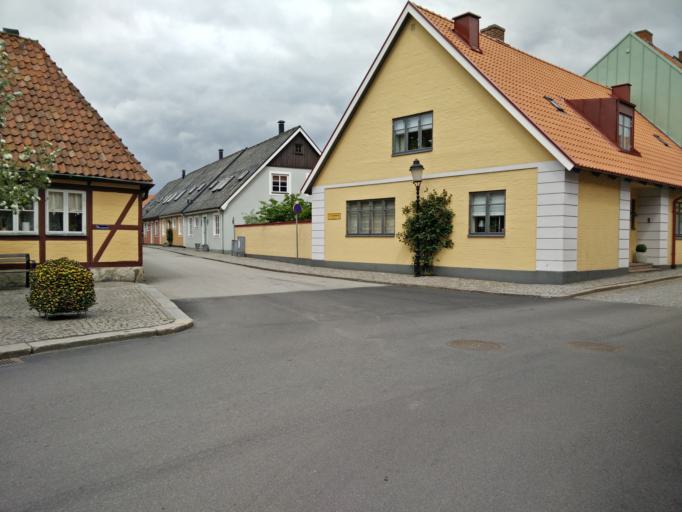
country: SE
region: Skane
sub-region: Ystads Kommun
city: Ystad
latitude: 55.4290
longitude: 13.8180
